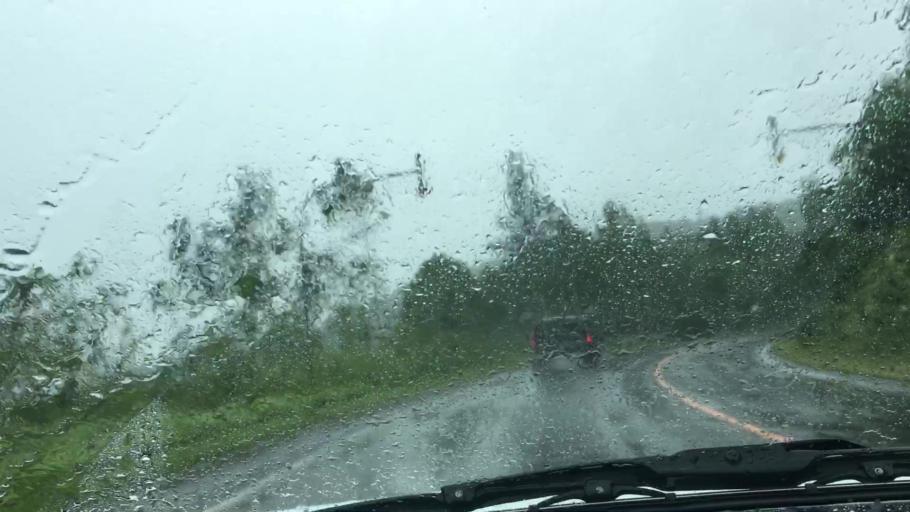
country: JP
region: Hokkaido
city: Sapporo
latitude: 42.8861
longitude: 141.1417
